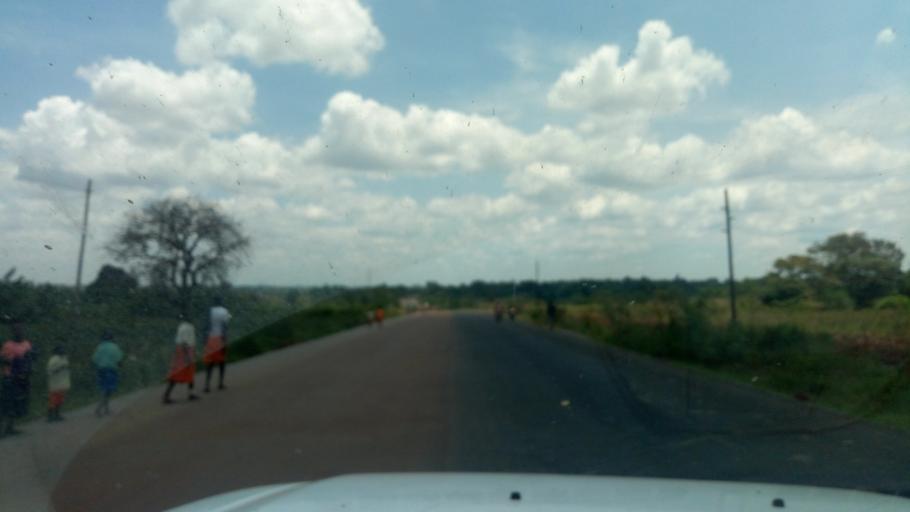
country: UG
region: Western Region
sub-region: Kiryandongo District
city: Kiryandongo
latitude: 1.7902
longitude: 31.9356
